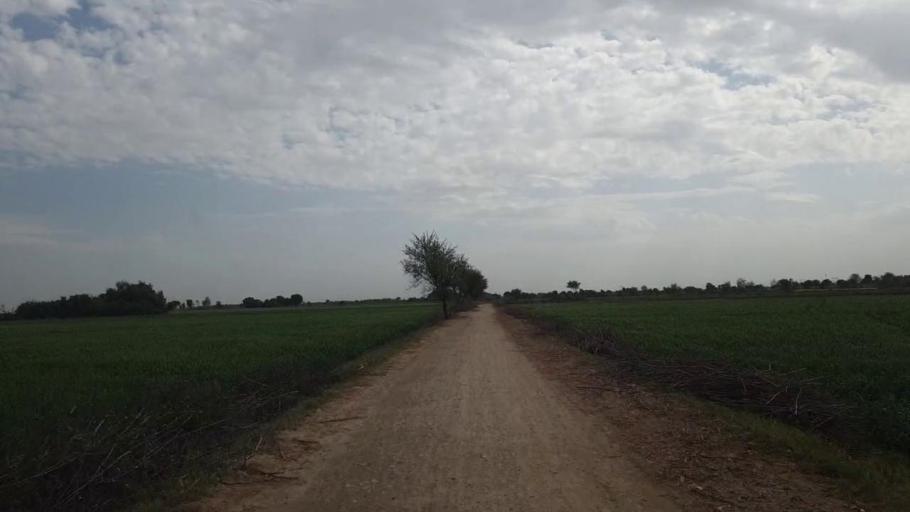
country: PK
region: Sindh
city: Hala
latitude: 25.9367
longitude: 68.4541
